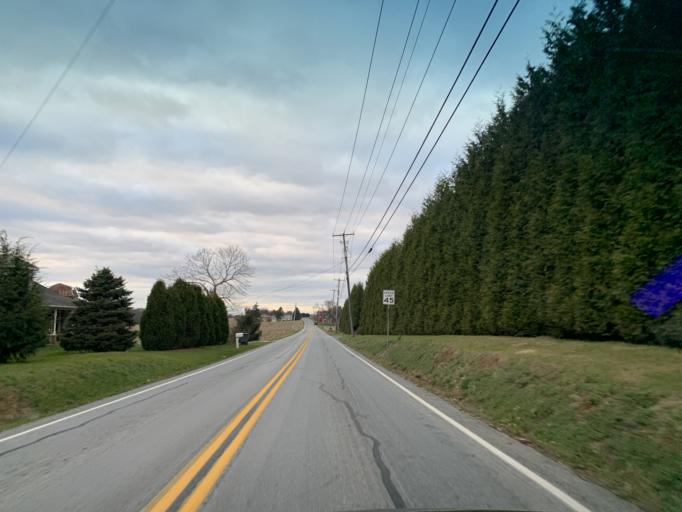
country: US
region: Pennsylvania
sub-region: York County
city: Shrewsbury
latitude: 39.7840
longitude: -76.6430
